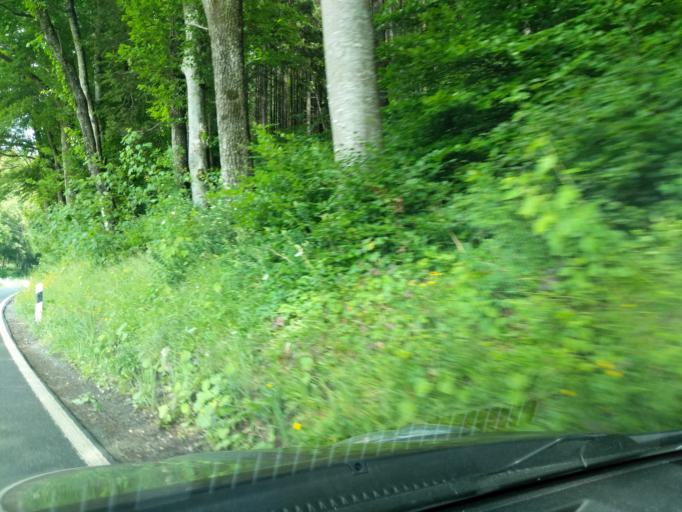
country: DE
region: Bavaria
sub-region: Upper Bavaria
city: Bruck
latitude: 48.0356
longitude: 11.9012
